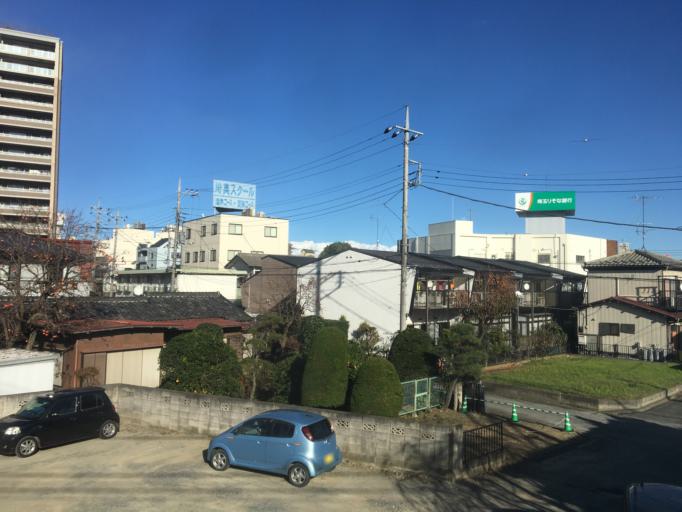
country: JP
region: Saitama
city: Fukiage-fujimi
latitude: 36.0378
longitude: 139.4001
